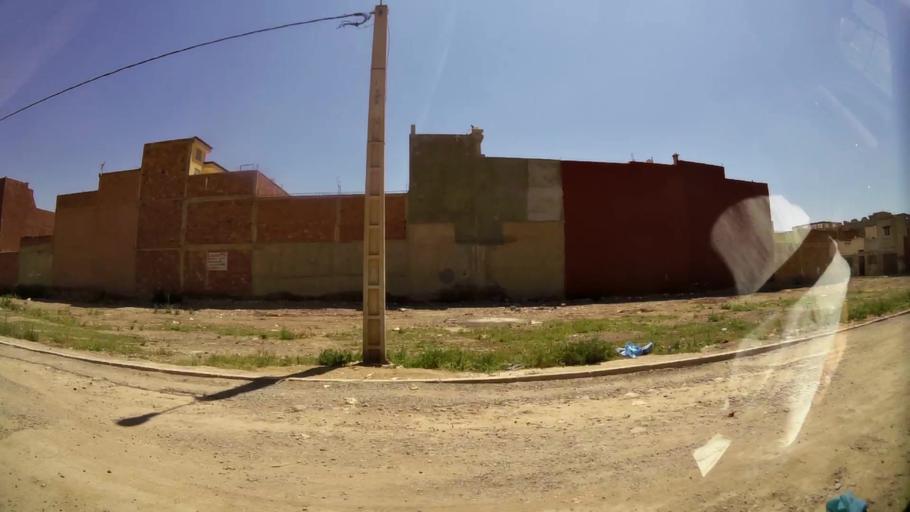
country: MA
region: Oriental
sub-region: Oujda-Angad
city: Oujda
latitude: 34.6911
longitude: -1.9343
